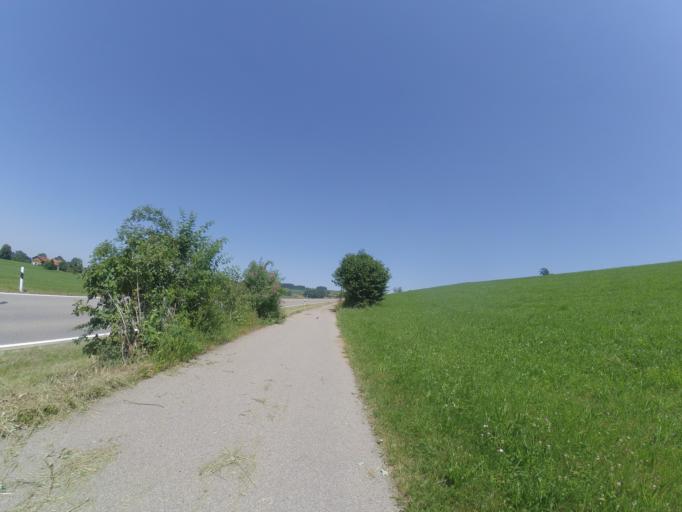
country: DE
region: Bavaria
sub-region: Swabia
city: Haldenwang
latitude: 47.8066
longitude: 10.3444
